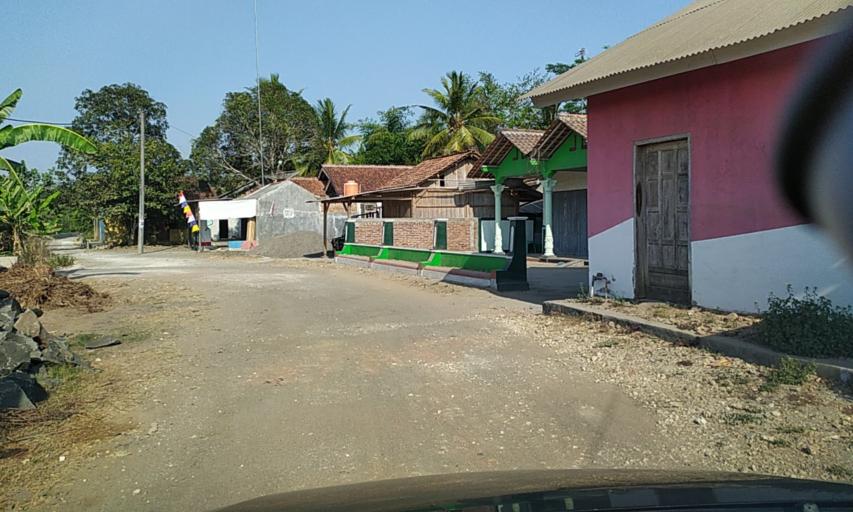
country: ID
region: Central Java
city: Wanadadi
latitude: -7.5482
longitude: 108.8149
